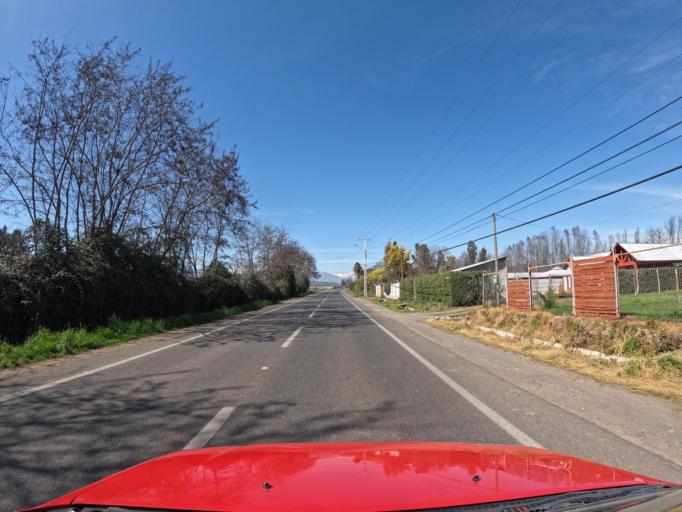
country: CL
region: Maule
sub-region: Provincia de Curico
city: Teno
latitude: -34.9654
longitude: -71.0412
